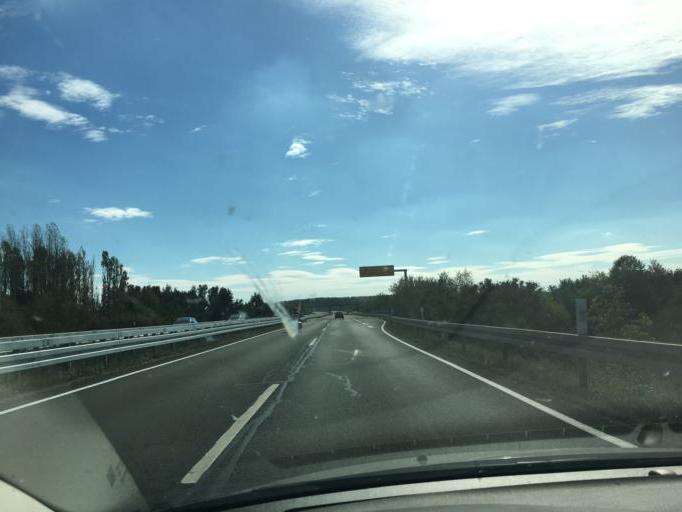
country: DE
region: Saxony-Anhalt
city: Wolmirstedt
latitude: 52.2476
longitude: 11.6021
